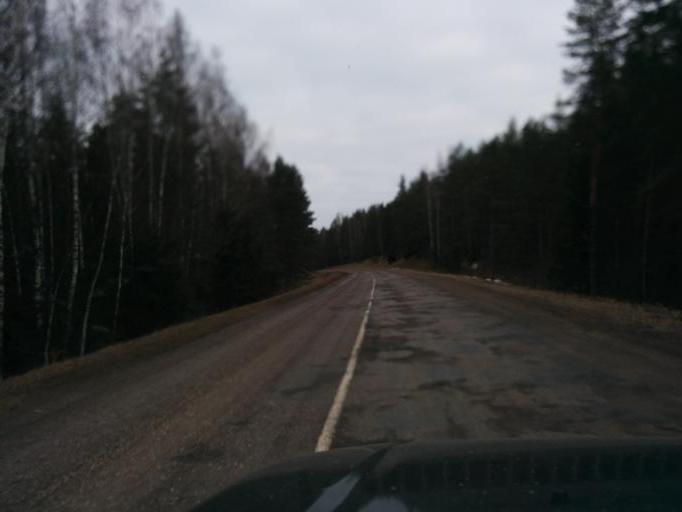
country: LV
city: Tireli
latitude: 56.8867
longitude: 23.5374
